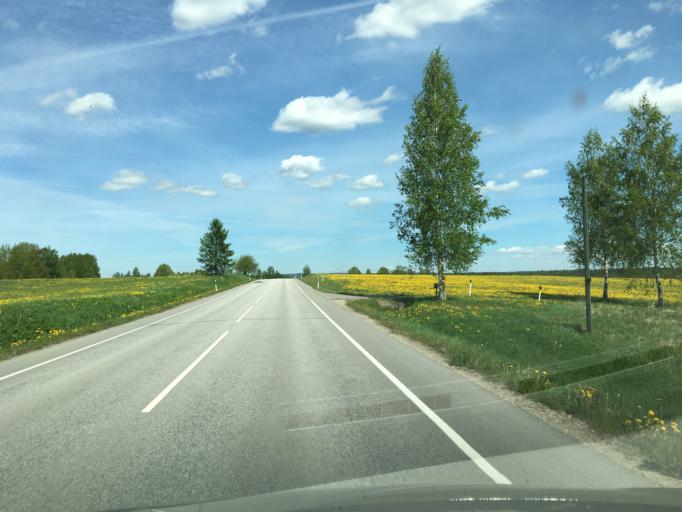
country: EE
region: Vorumaa
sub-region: Antsla vald
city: Vana-Antsla
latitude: 57.8795
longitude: 26.2803
